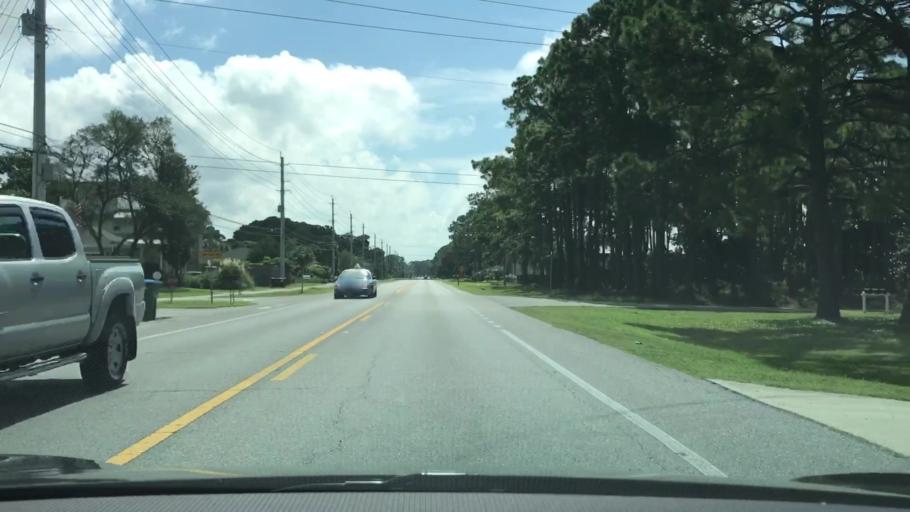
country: US
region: Florida
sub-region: Bay County
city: Lower Grand Lagoon
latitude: 30.1614
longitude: -85.7655
